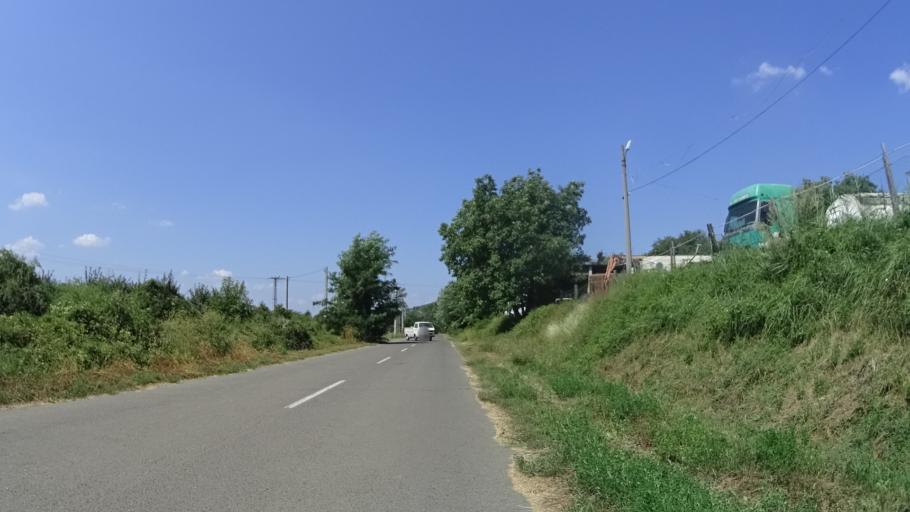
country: HU
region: Pest
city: Dunabogdany
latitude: 47.8104
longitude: 19.0921
